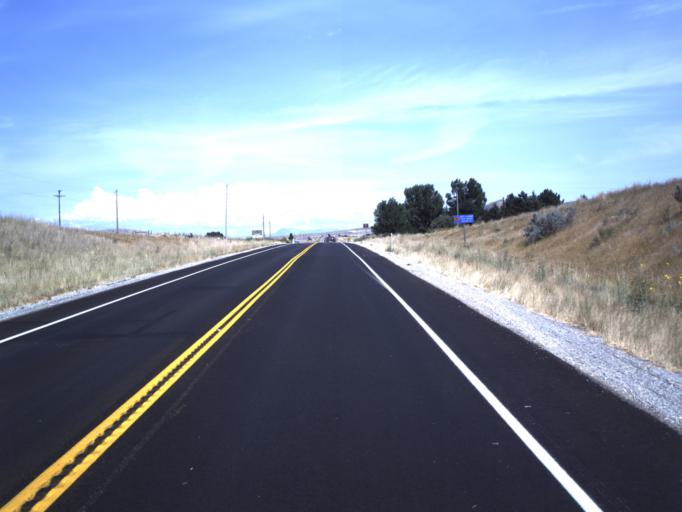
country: US
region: Utah
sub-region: Box Elder County
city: Garland
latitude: 41.7835
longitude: -112.1044
